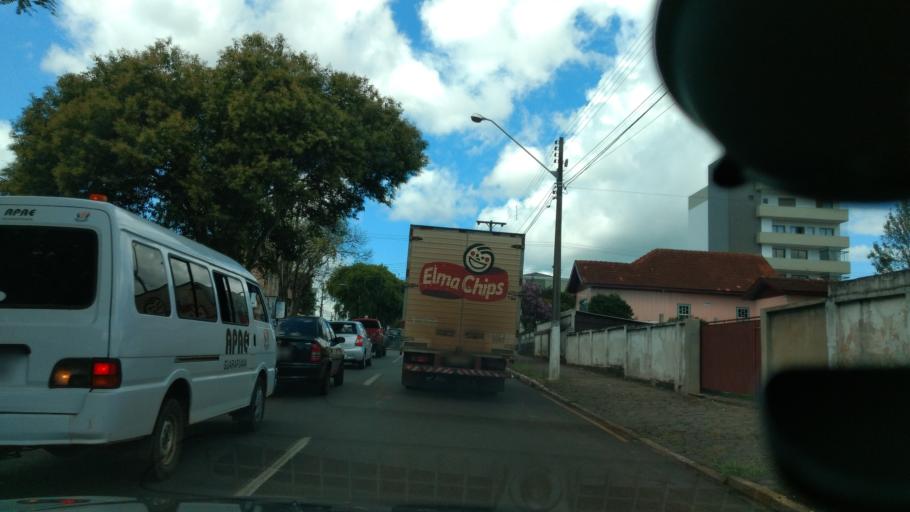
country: BR
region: Parana
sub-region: Guarapuava
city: Guarapuava
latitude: -25.3893
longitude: -51.4764
